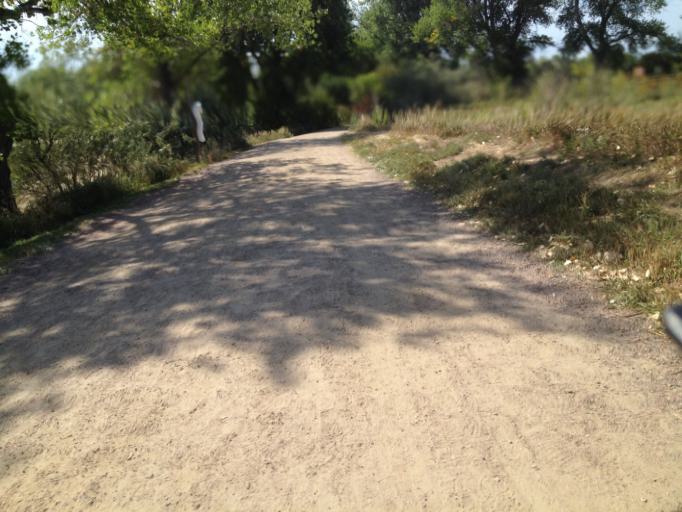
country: US
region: Colorado
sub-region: Boulder County
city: Lafayette
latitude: 39.9972
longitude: -105.1112
